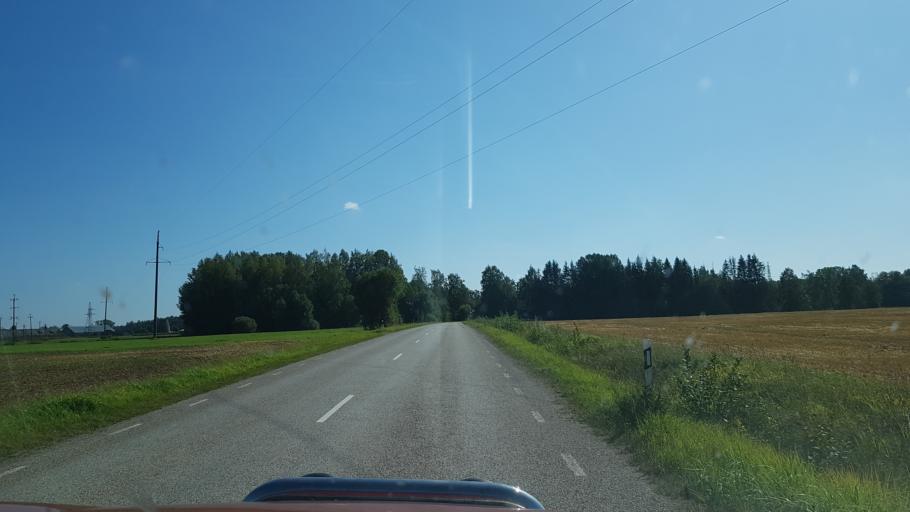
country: EE
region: Polvamaa
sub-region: Polva linn
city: Polva
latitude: 58.2130
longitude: 27.2518
